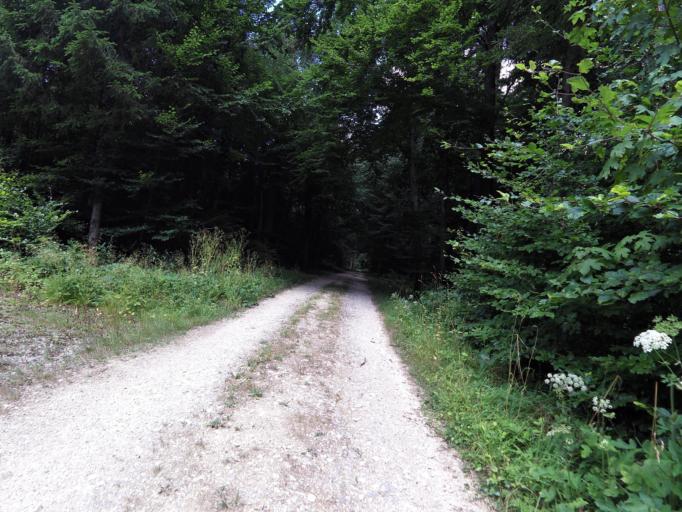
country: CH
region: Thurgau
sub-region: Kreuzlingen District
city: Tagerwilen
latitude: 47.6403
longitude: 9.1070
